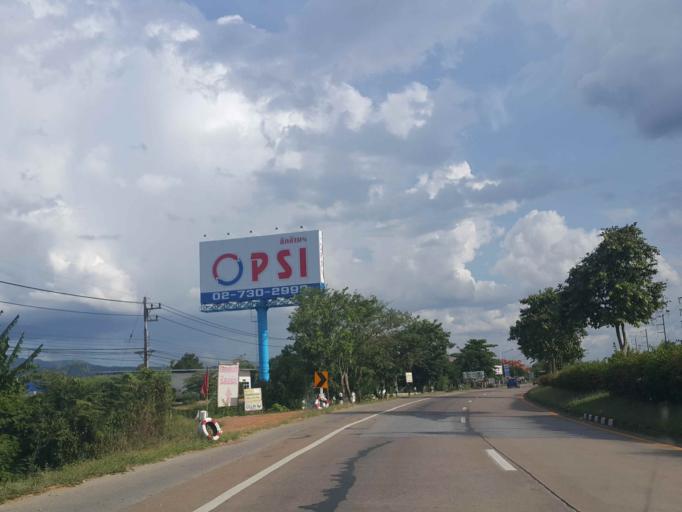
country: TH
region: Phrae
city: Sung Men
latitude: 18.0253
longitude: 100.1110
